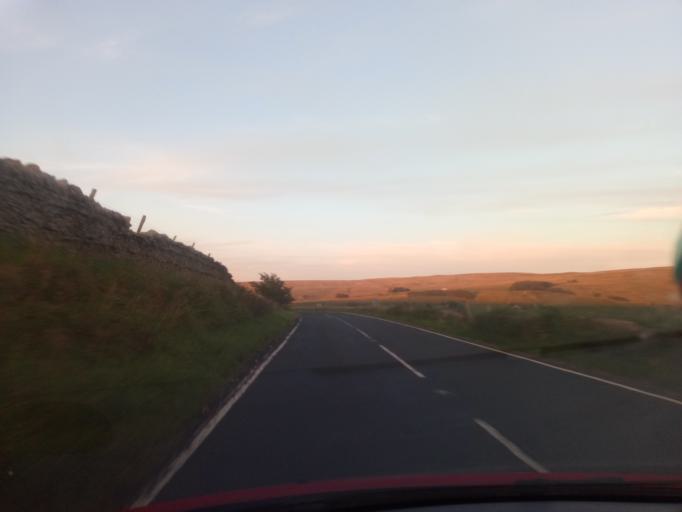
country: GB
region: England
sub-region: Northumberland
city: Bardon Mill
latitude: 54.8653
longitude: -2.3597
